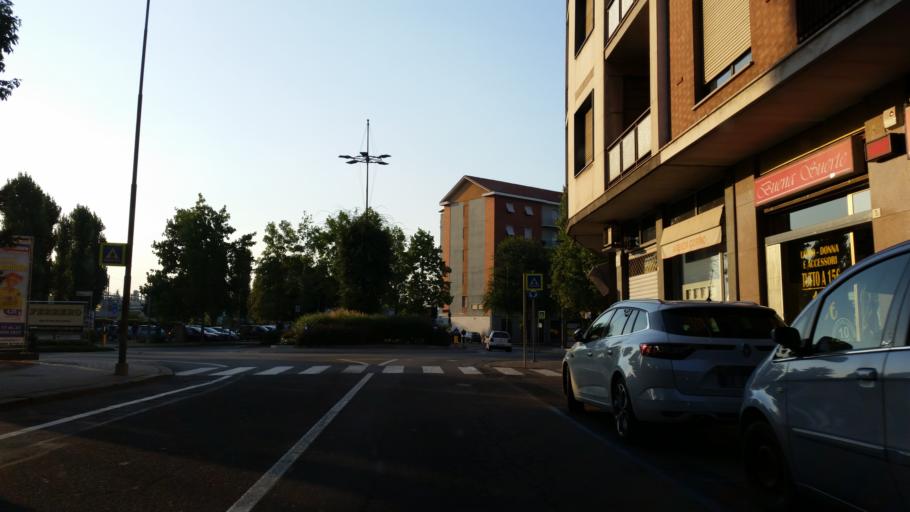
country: IT
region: Piedmont
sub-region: Provincia di Cuneo
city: Alba
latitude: 44.6988
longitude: 8.0306
